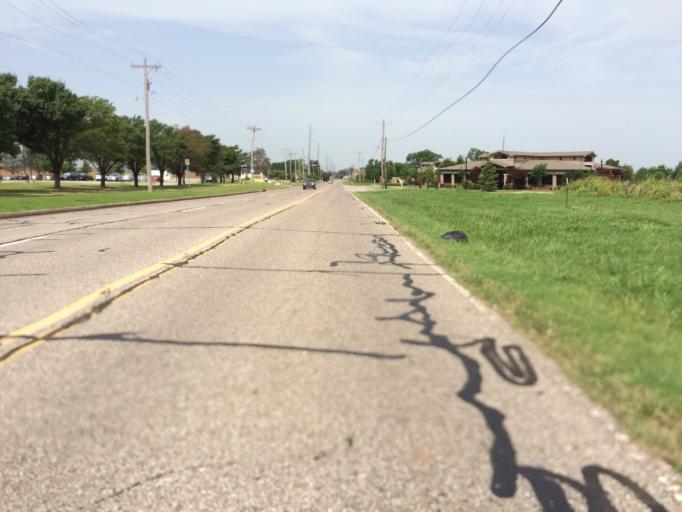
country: US
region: Oklahoma
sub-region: Cleveland County
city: Norman
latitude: 35.1897
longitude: -97.4114
